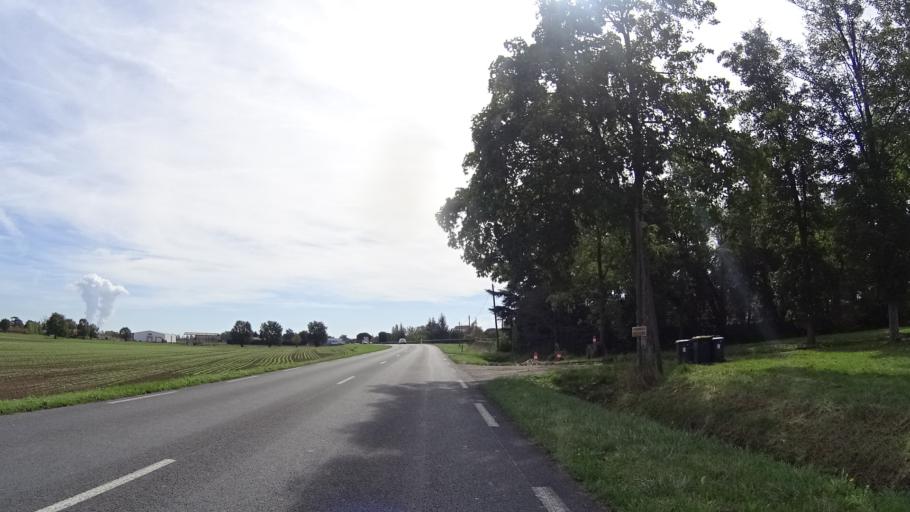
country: FR
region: Aquitaine
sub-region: Departement du Lot-et-Garonne
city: Boe
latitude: 44.1663
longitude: 0.6436
